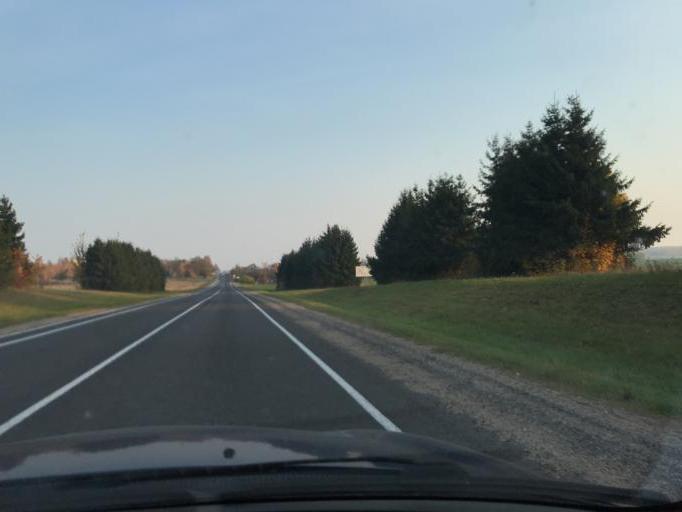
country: BY
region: Grodnenskaya
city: Karelichy
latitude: 53.5801
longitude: 26.1227
